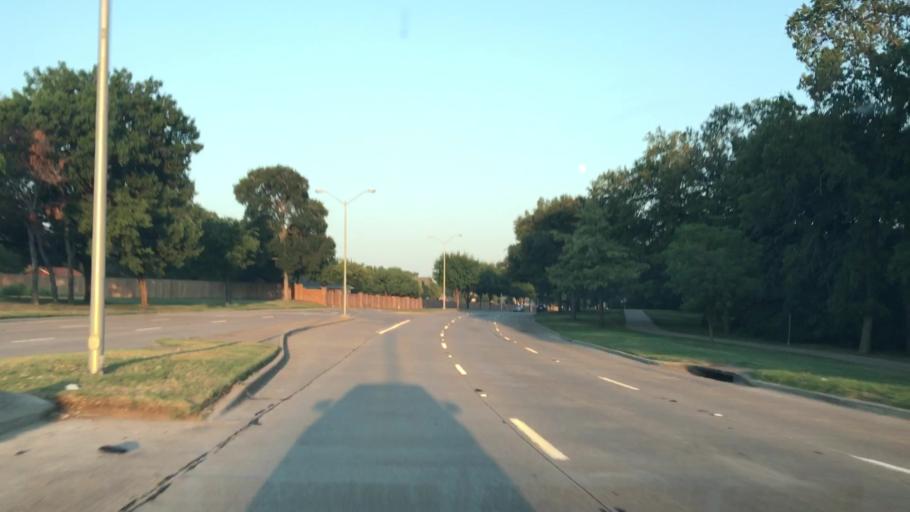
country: US
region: Texas
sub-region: Dallas County
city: Richardson
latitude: 32.8984
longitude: -96.7621
